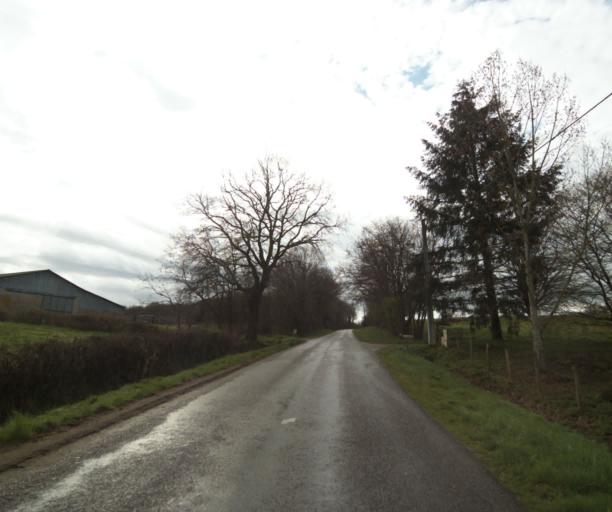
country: FR
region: Auvergne
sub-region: Departement de l'Allier
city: Toulon-sur-Allier
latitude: 46.5234
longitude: 3.4171
